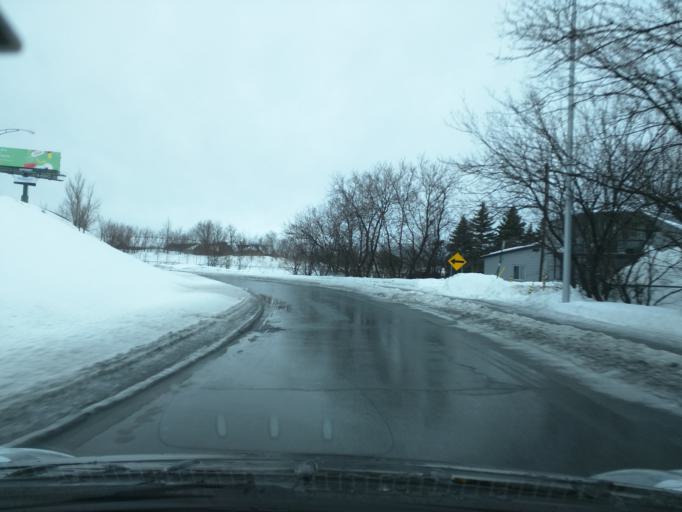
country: CA
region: Quebec
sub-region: Monteregie
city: Longueuil
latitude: 45.5057
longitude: -73.4909
